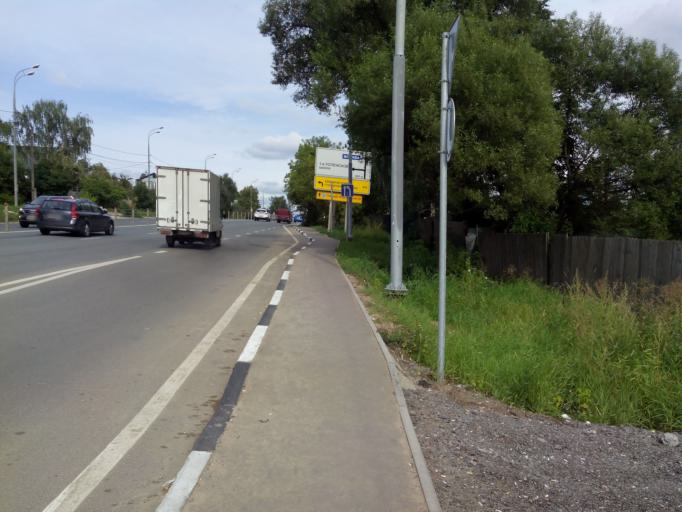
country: RU
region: Moskovskaya
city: Lesnoy Gorodok
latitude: 55.6578
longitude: 37.1822
